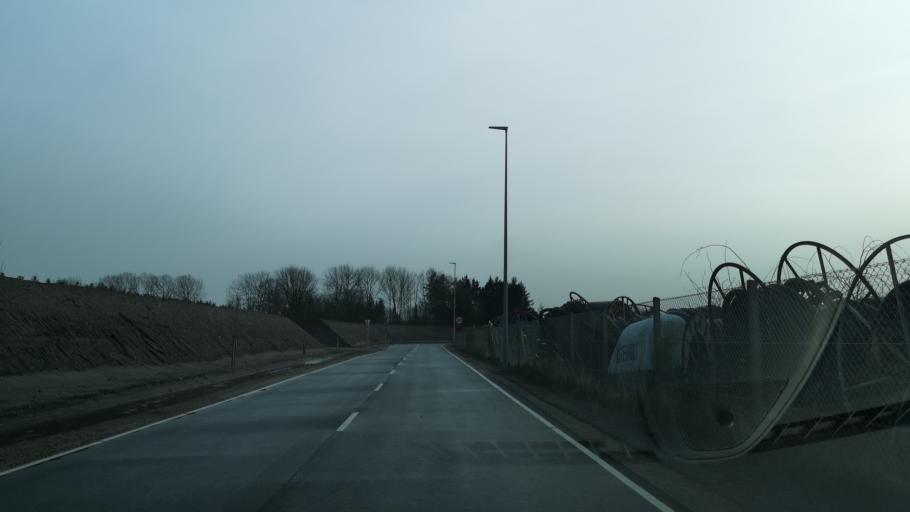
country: DK
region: Central Jutland
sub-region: Ikast-Brande Kommune
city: Brande
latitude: 56.0059
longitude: 9.1198
